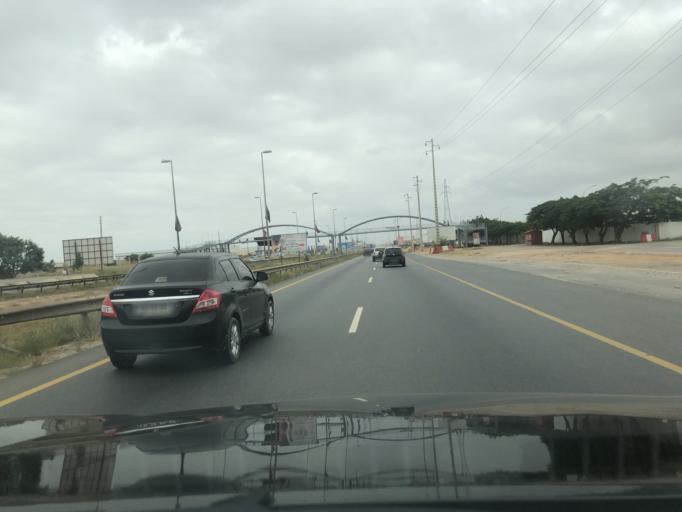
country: AO
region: Luanda
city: Luanda
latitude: -8.9733
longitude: 13.2346
